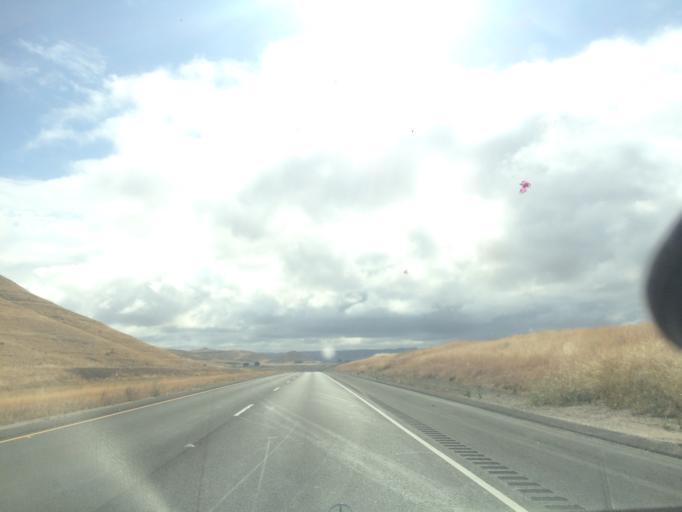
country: US
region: California
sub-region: San Luis Obispo County
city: Shandon
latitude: 35.6607
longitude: -120.4481
